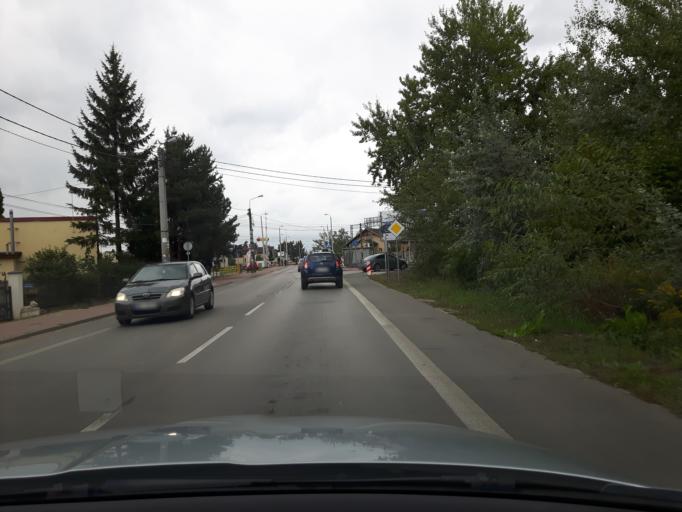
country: PL
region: Masovian Voivodeship
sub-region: Powiat wolominski
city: Kobylka
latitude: 52.3253
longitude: 21.1911
